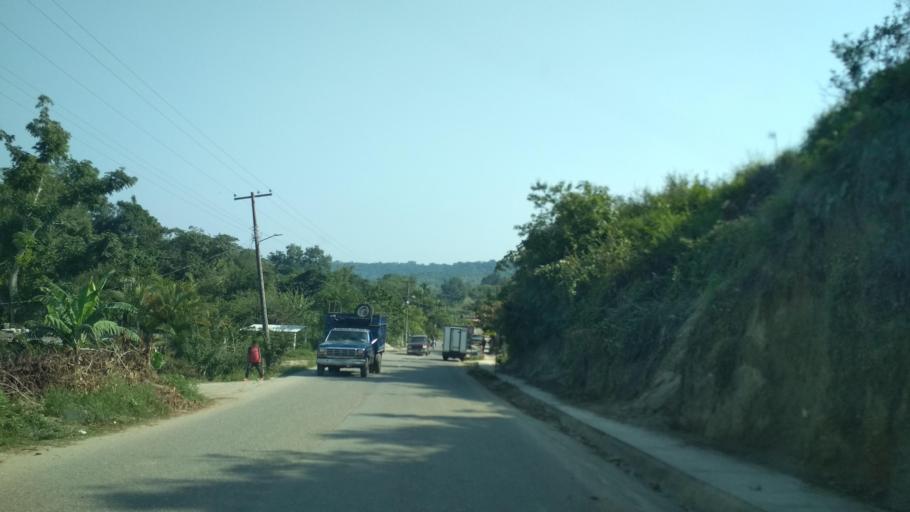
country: MX
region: Puebla
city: San Jose Acateno
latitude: 20.1833
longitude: -97.2619
